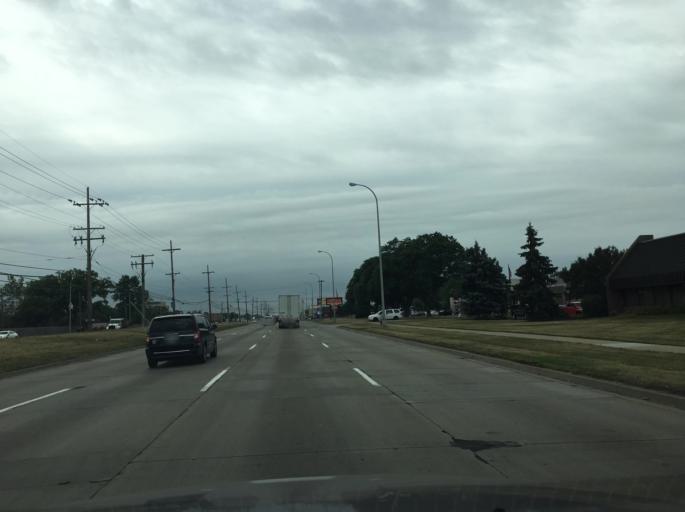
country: US
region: Michigan
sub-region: Macomb County
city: Center Line
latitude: 42.5032
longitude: -83.0466
